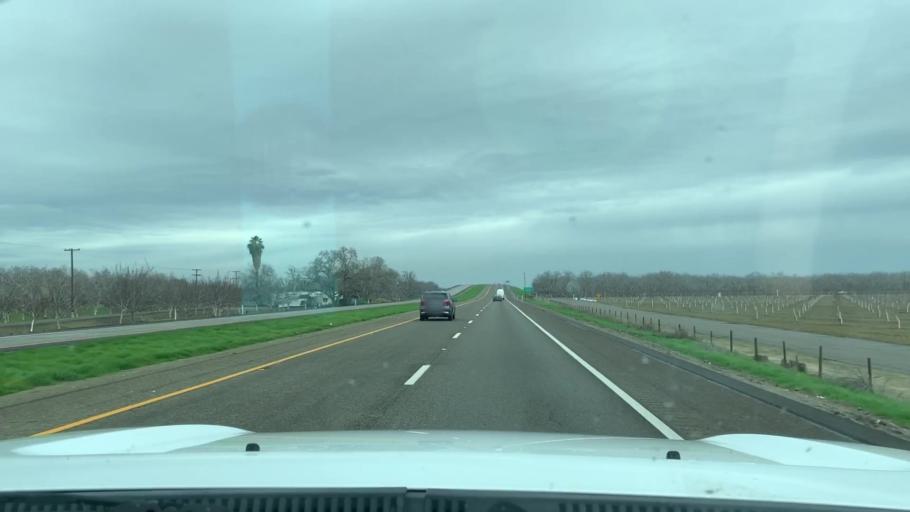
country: US
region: California
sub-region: Fresno County
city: Riverdale
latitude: 36.3917
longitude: -119.8090
